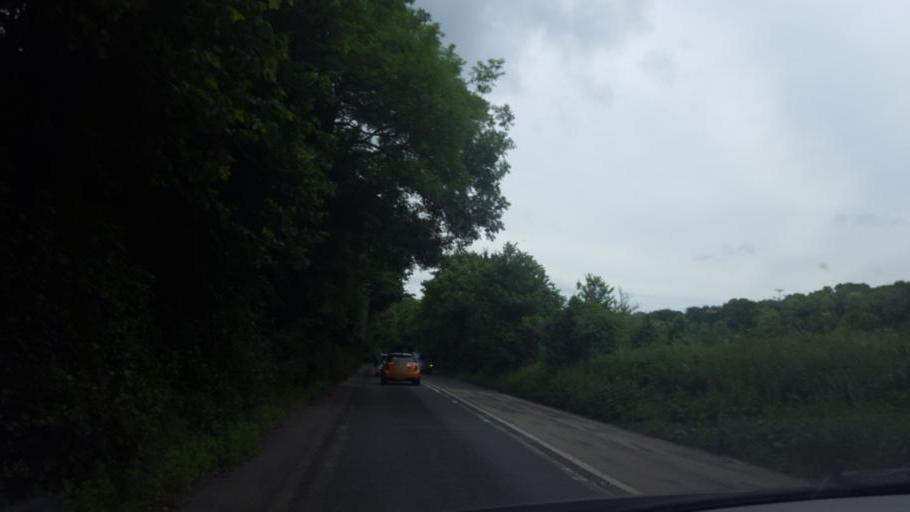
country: GB
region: England
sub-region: Royal Borough of Windsor and Maidenhead
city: Hurley
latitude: 51.5410
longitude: -0.8080
